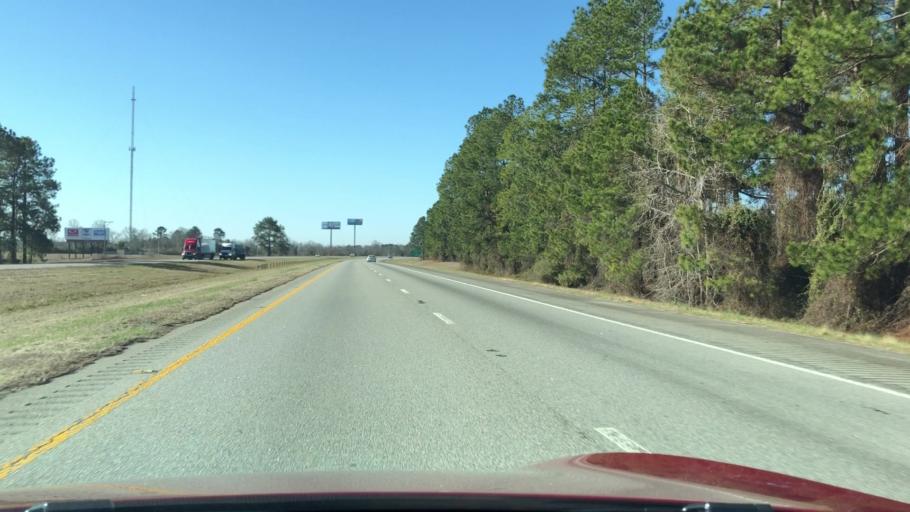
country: US
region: South Carolina
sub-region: Clarendon County
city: Manning
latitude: 33.6032
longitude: -80.3247
